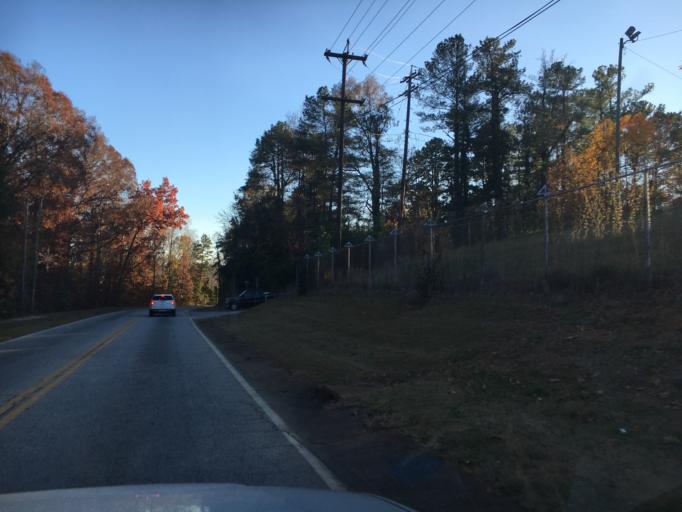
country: US
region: South Carolina
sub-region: Spartanburg County
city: Lyman
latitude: 34.9437
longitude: -82.1220
